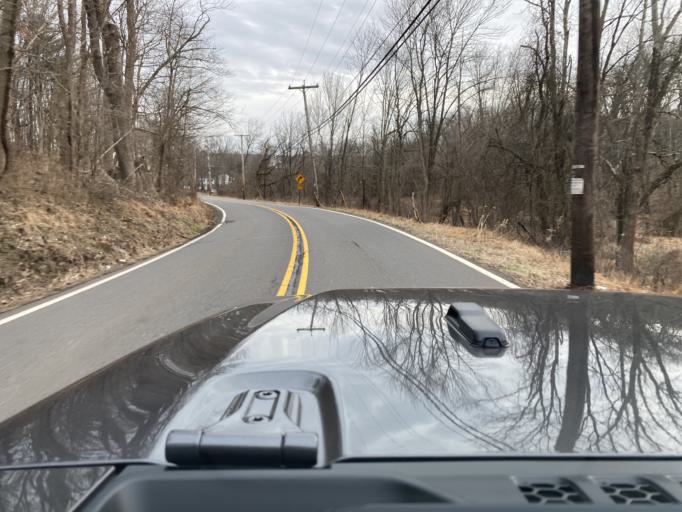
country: US
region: New Jersey
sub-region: Somerset County
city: Bloomingdale
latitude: 40.5014
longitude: -74.7213
